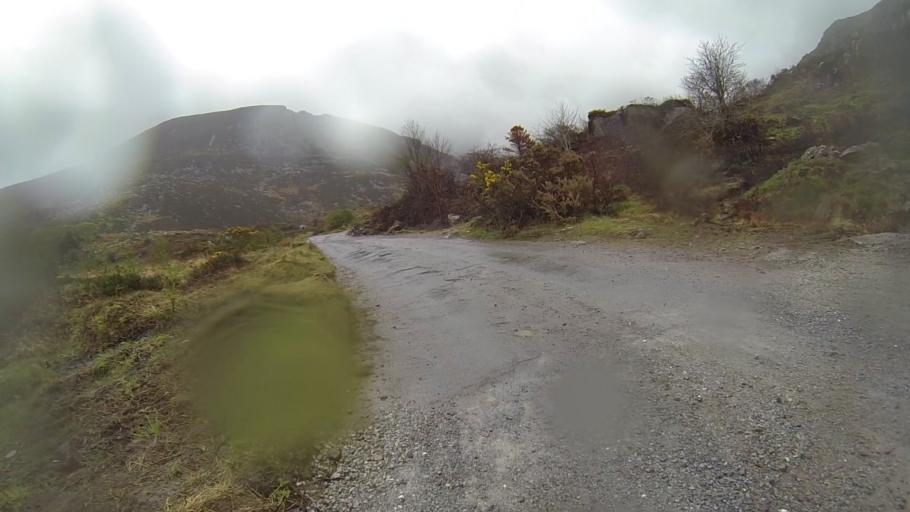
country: IE
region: Munster
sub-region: Ciarrai
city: Cill Airne
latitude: 52.0363
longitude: -9.6364
